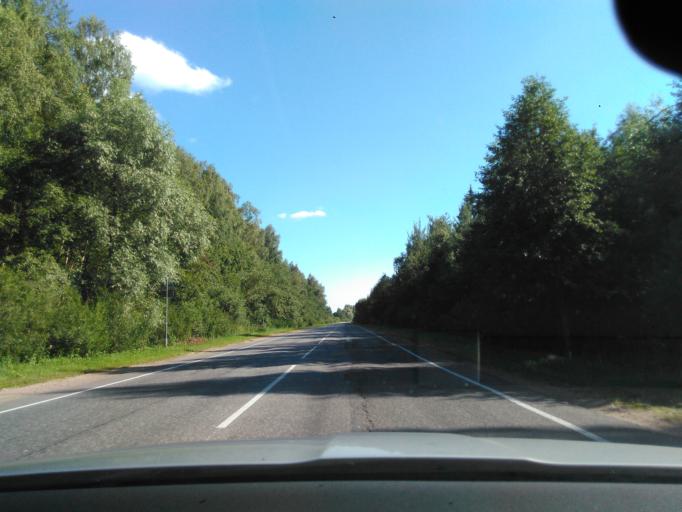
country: RU
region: Tverskaya
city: Konakovo
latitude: 56.6485
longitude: 36.7086
